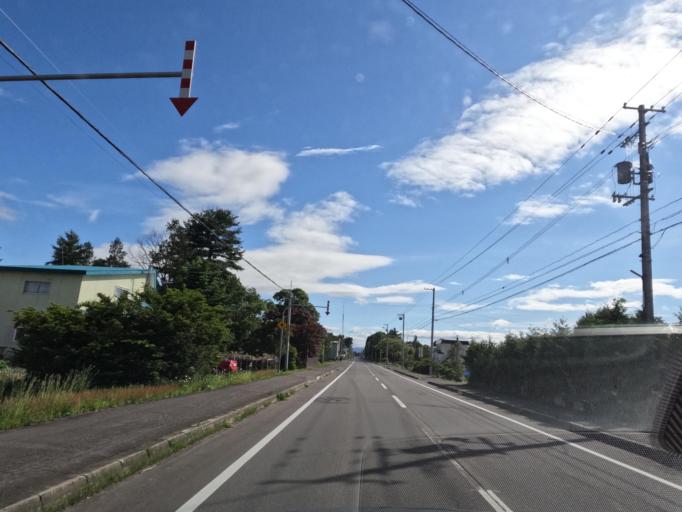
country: JP
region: Hokkaido
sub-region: Asahikawa-shi
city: Asahikawa
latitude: 43.7013
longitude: 142.5116
